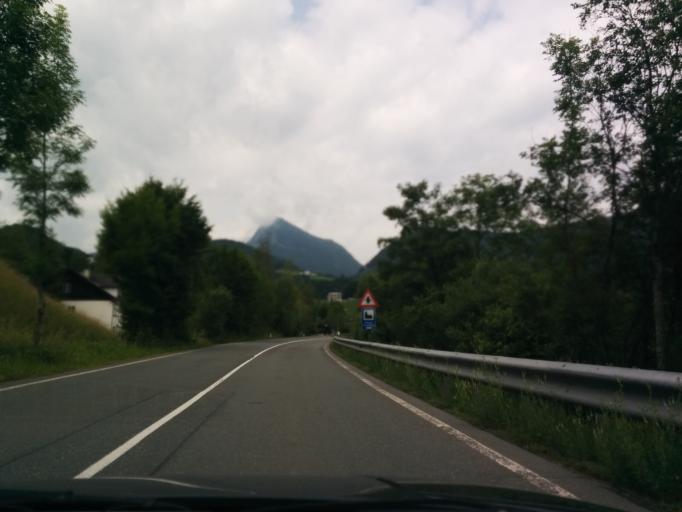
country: AT
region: Salzburg
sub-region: Politischer Bezirk Hallein
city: Abtenau
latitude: 47.5931
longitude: 13.3136
